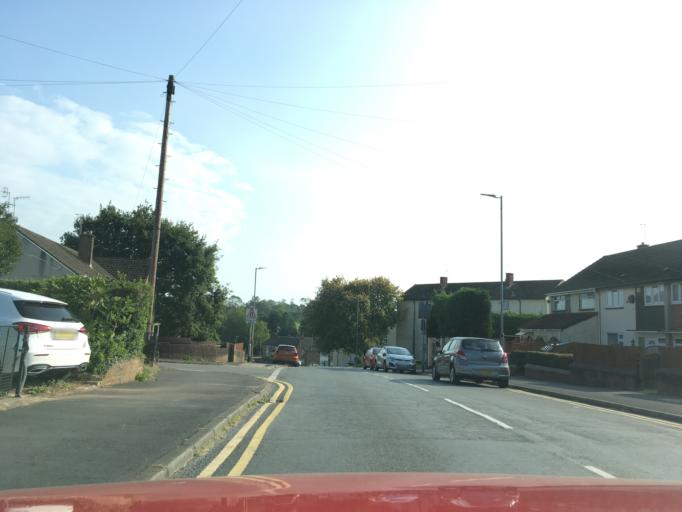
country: GB
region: Wales
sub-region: Newport
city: Newport
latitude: 51.6093
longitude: -3.0361
